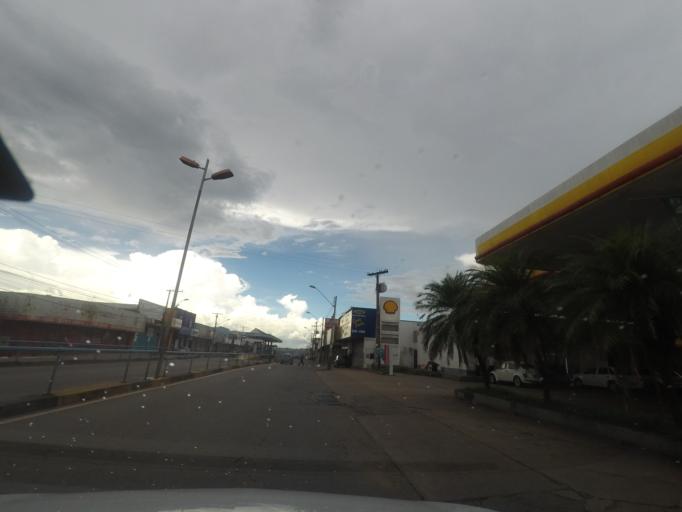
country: BR
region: Goias
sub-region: Goiania
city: Goiania
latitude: -16.6711
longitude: -49.2320
